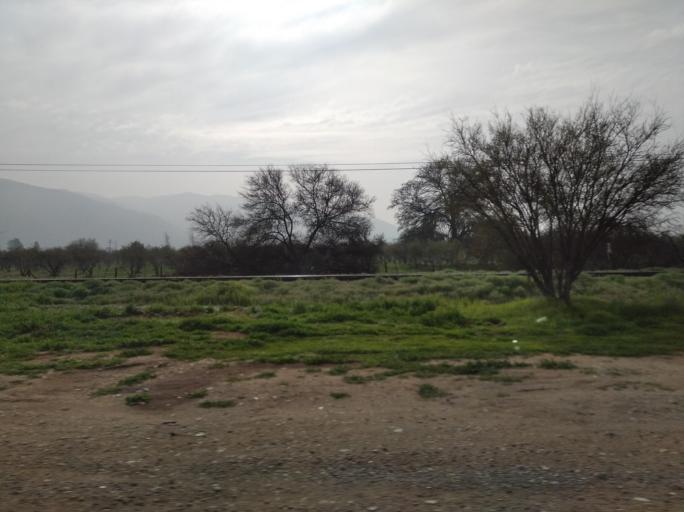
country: CL
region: Santiago Metropolitan
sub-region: Provincia de Chacabuco
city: Lampa
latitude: -33.1560
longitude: -70.9002
